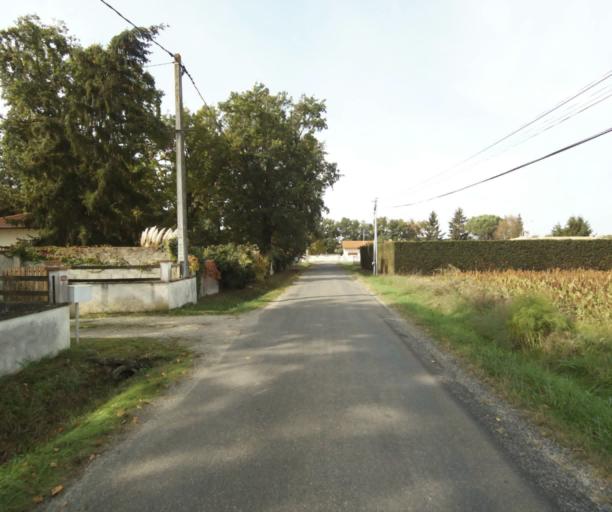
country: FR
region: Midi-Pyrenees
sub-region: Departement du Tarn-et-Garonne
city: Orgueil
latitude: 43.9113
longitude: 1.3959
